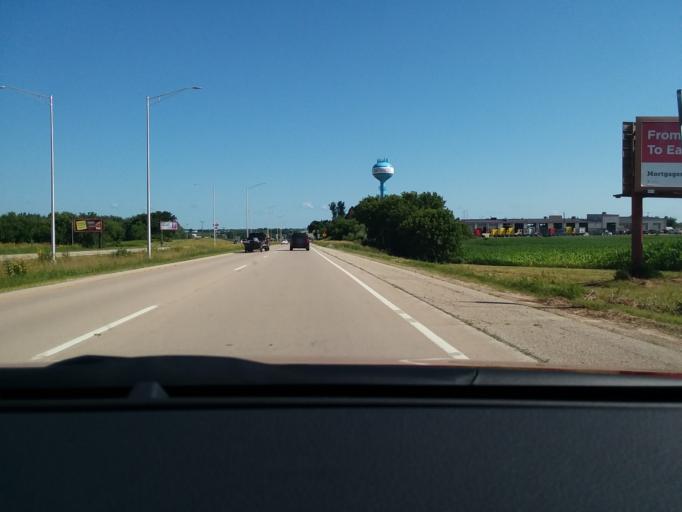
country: US
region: Wisconsin
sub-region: Dane County
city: Windsor
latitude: 43.1680
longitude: -89.3242
